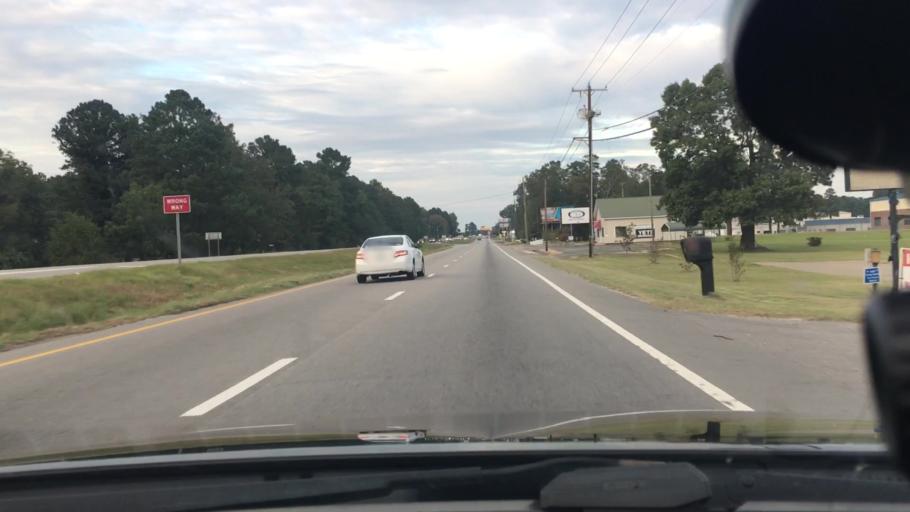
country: US
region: North Carolina
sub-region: Lee County
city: Sanford
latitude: 35.4226
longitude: -79.2258
